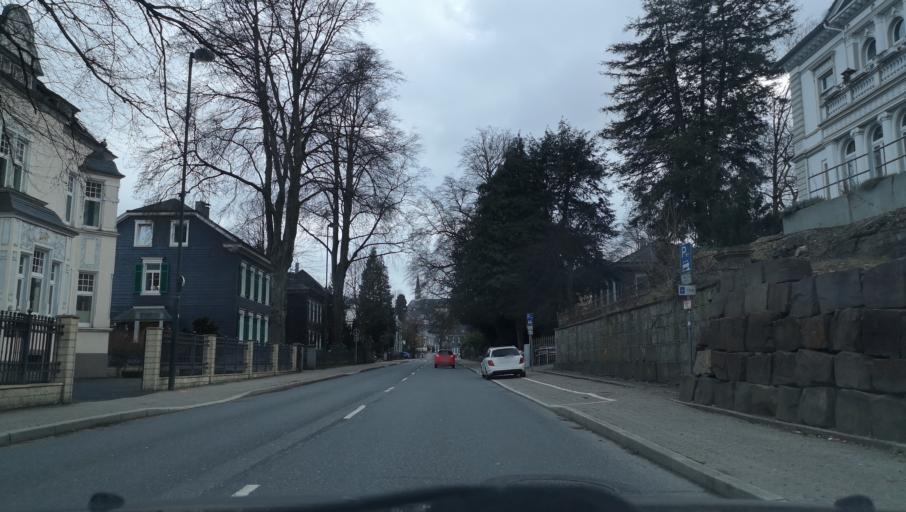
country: DE
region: North Rhine-Westphalia
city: Huckeswagen
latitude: 51.1512
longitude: 7.3391
